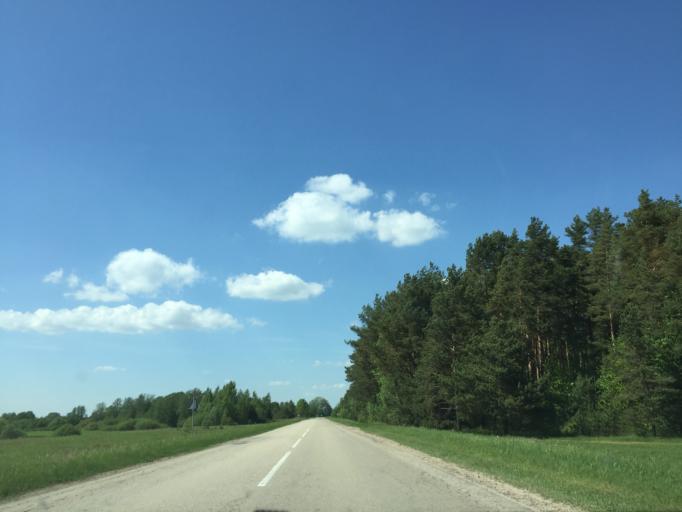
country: LV
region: Ozolnieku
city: Ozolnieki
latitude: 56.6122
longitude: 23.9403
